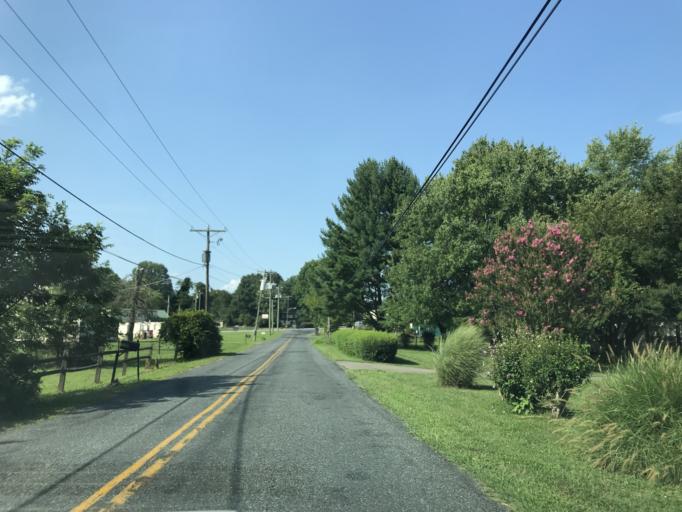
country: US
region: Maryland
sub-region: Harford County
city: South Bel Air
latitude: 39.6298
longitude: -76.2743
